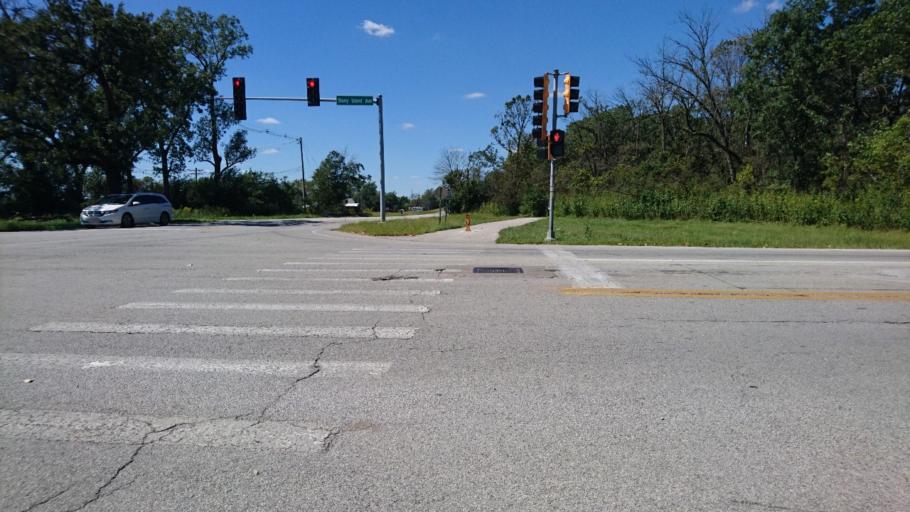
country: US
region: Illinois
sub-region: Cook County
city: Glenwood
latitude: 41.5428
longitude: -87.5780
